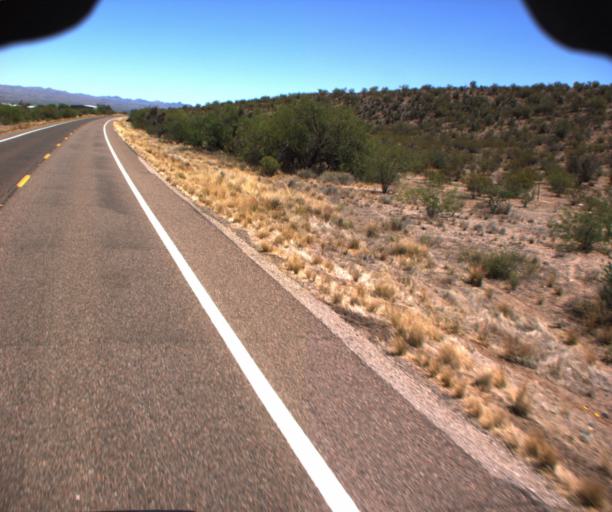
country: US
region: Arizona
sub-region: Maricopa County
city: Wickenburg
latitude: 33.9651
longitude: -112.8183
